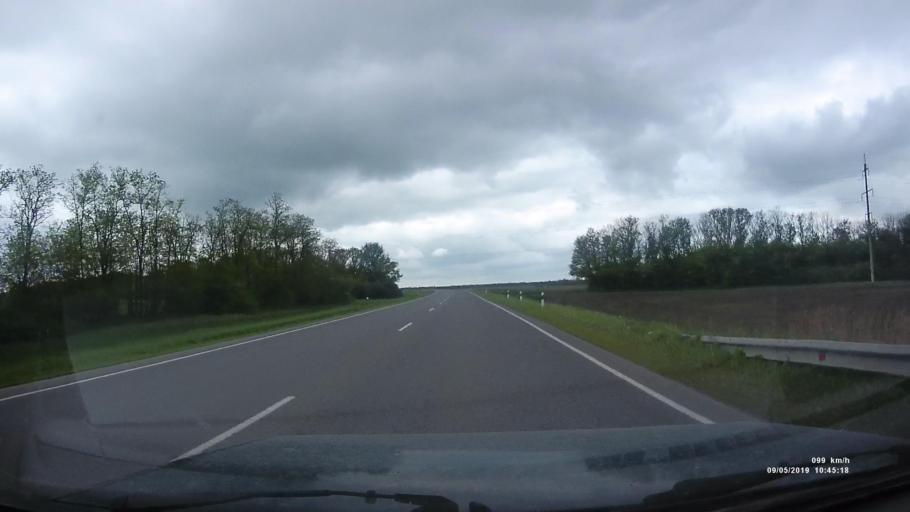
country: RU
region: Rostov
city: Peshkovo
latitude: 46.9962
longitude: 39.3702
